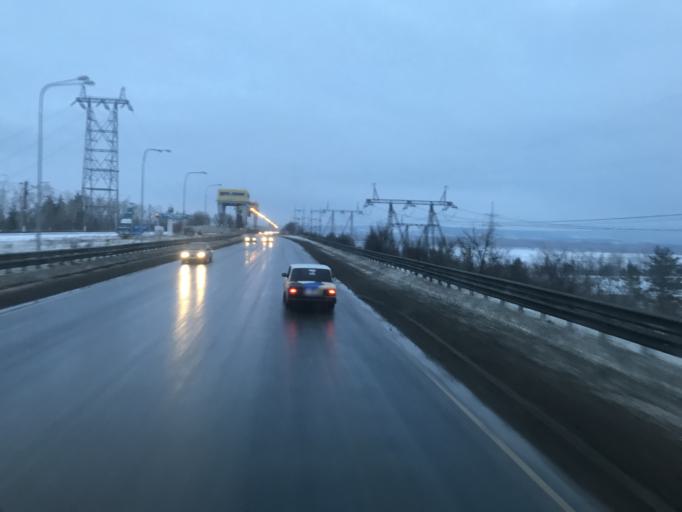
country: RU
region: Samara
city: Zhigulevsk
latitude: 53.4551
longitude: 49.4949
